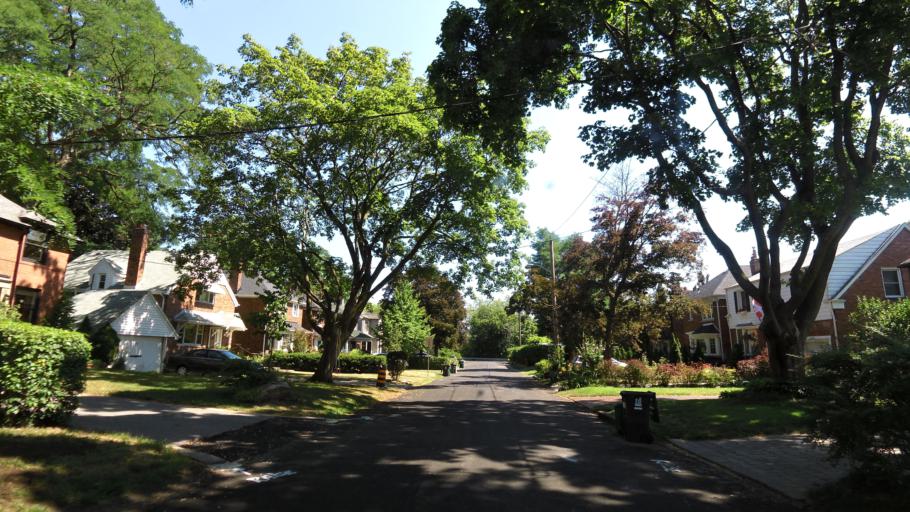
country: CA
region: Ontario
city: Etobicoke
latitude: 43.6545
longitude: -79.4939
